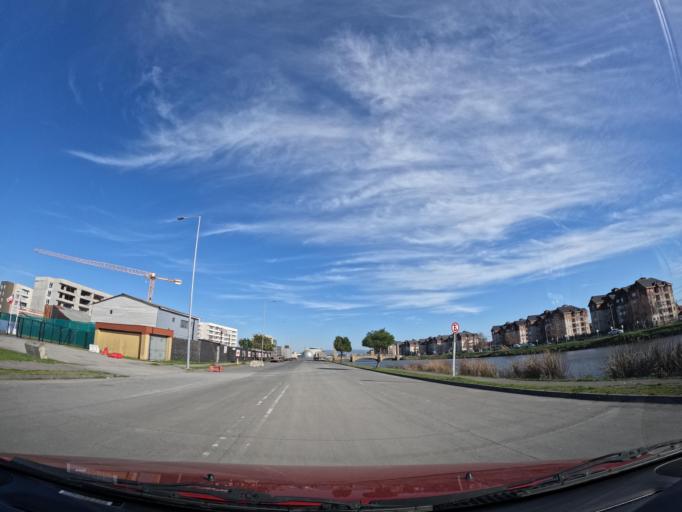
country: CL
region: Biobio
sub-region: Provincia de Concepcion
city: Talcahuano
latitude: -36.7677
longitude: -73.0747
